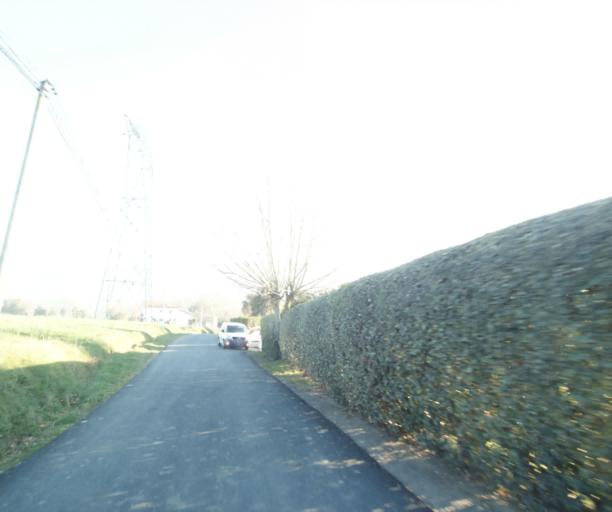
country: FR
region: Aquitaine
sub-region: Departement des Pyrenees-Atlantiques
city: Urrugne
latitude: 43.3440
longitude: -1.7016
